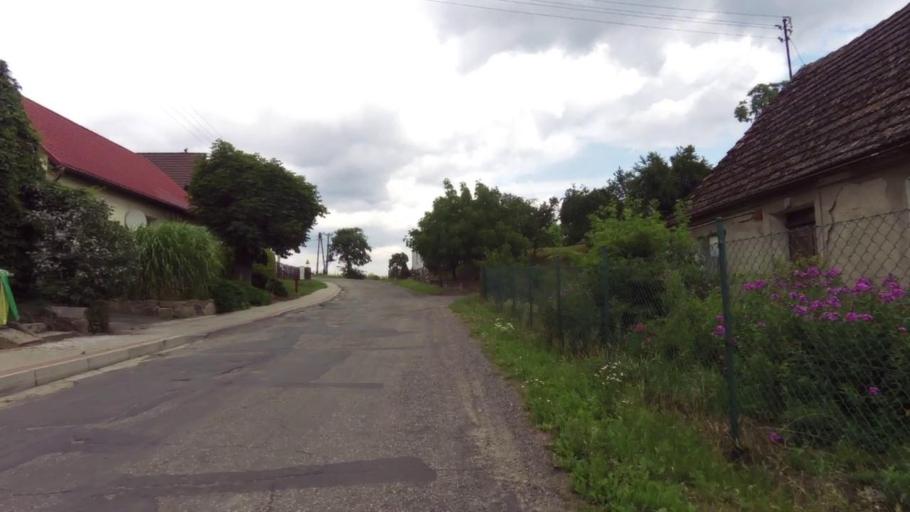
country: PL
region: West Pomeranian Voivodeship
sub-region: Powiat gryfinski
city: Moryn
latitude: 52.8722
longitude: 14.3900
